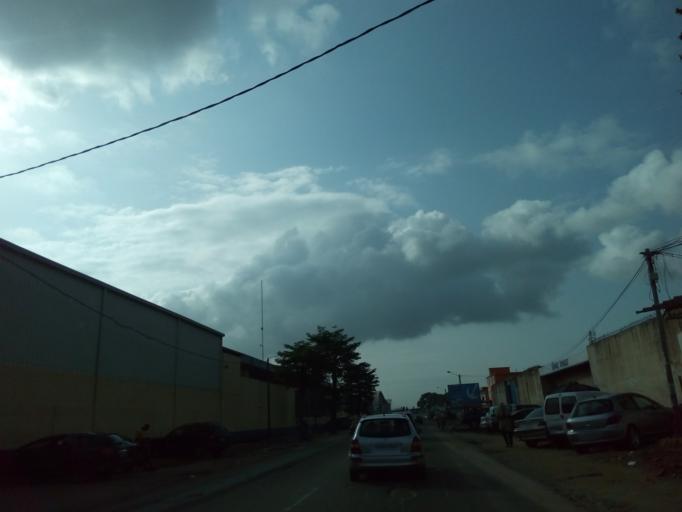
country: CI
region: Lagunes
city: Abidjan
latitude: 5.2941
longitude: -4.0012
